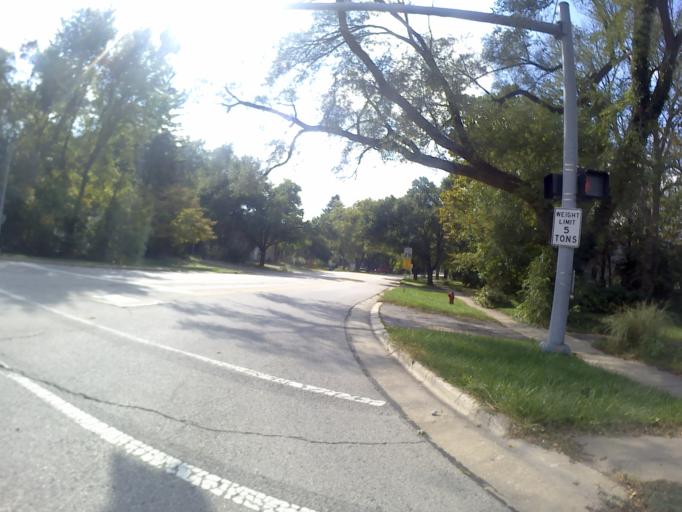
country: US
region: Illinois
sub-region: DuPage County
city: Lisle
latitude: 41.7979
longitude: -88.0776
